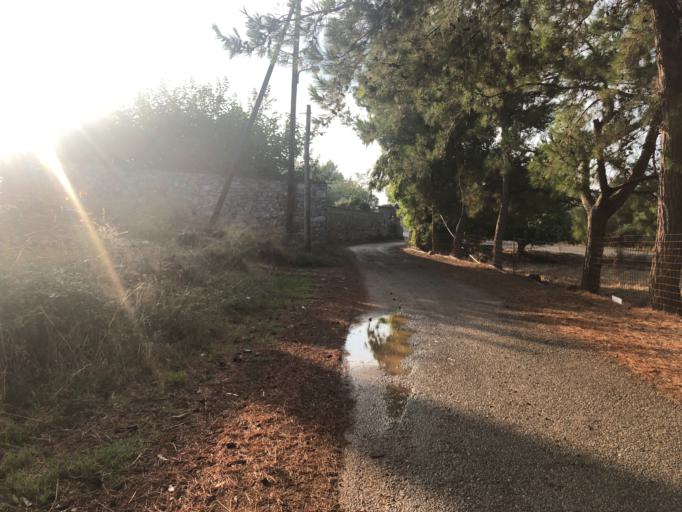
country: GR
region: Crete
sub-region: Nomos Chanias
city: Georgioupolis
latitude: 35.3451
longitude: 24.3090
